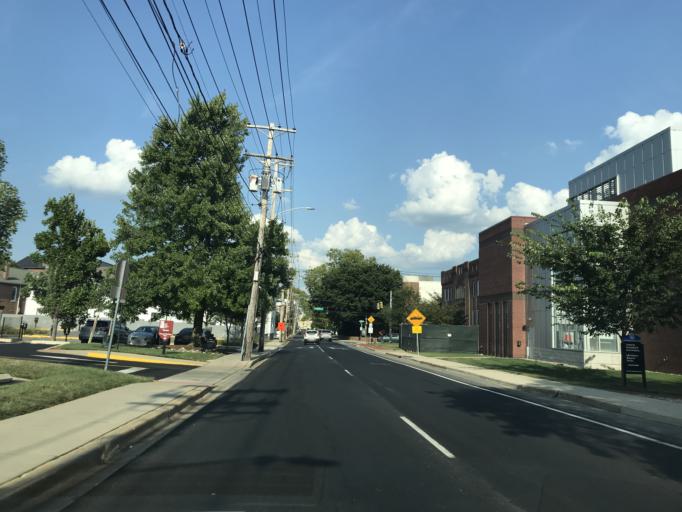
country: US
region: Delaware
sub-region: New Castle County
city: Newark
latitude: 39.6819
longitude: -75.7506
